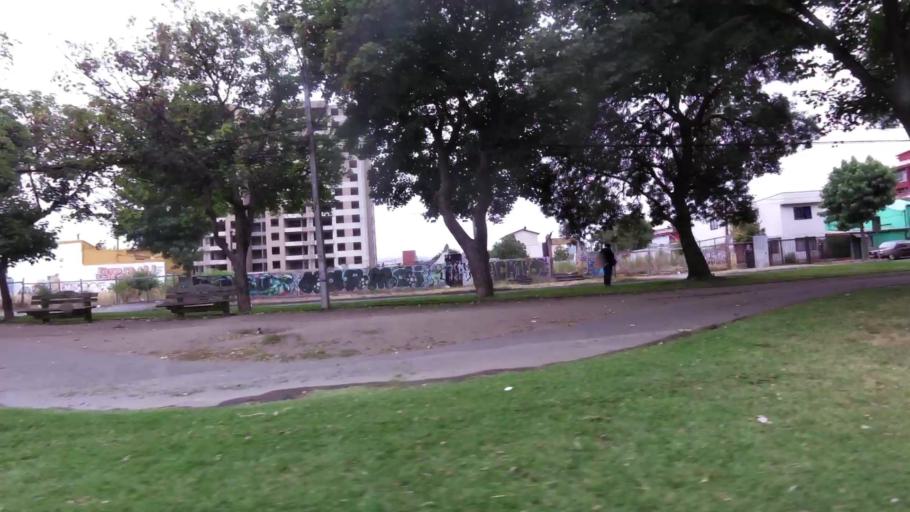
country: CL
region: Biobio
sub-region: Provincia de Concepcion
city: Concepcion
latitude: -36.8199
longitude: -73.0627
